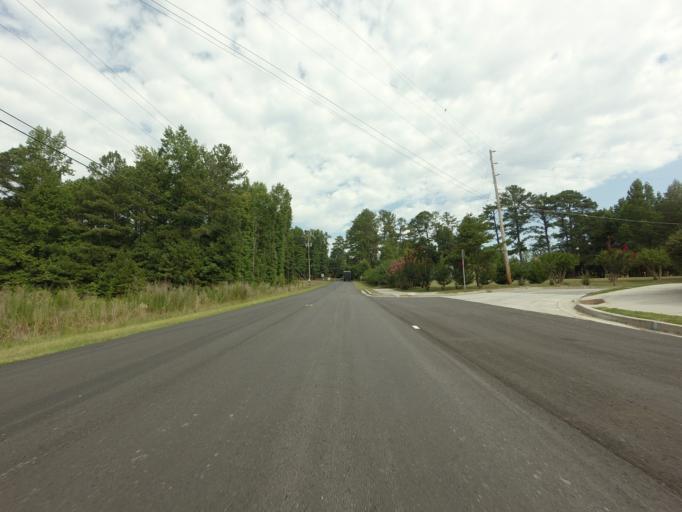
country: US
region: Georgia
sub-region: Gwinnett County
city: Duluth
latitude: 34.0497
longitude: -84.1331
